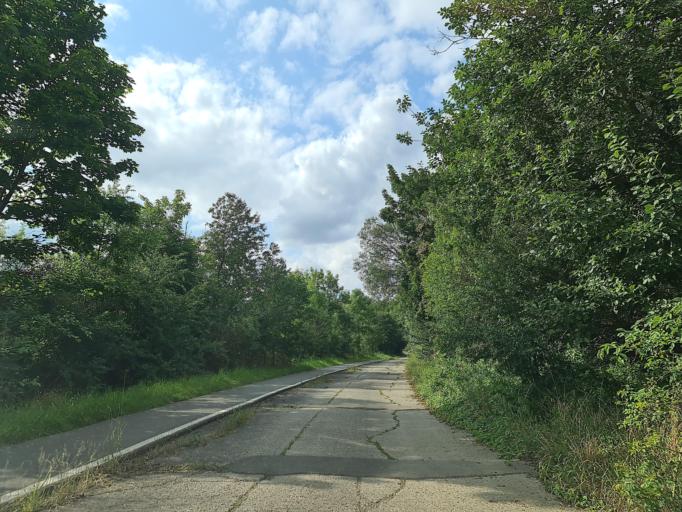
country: DE
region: Saxony
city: Syrau
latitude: 50.4989
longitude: 12.0764
